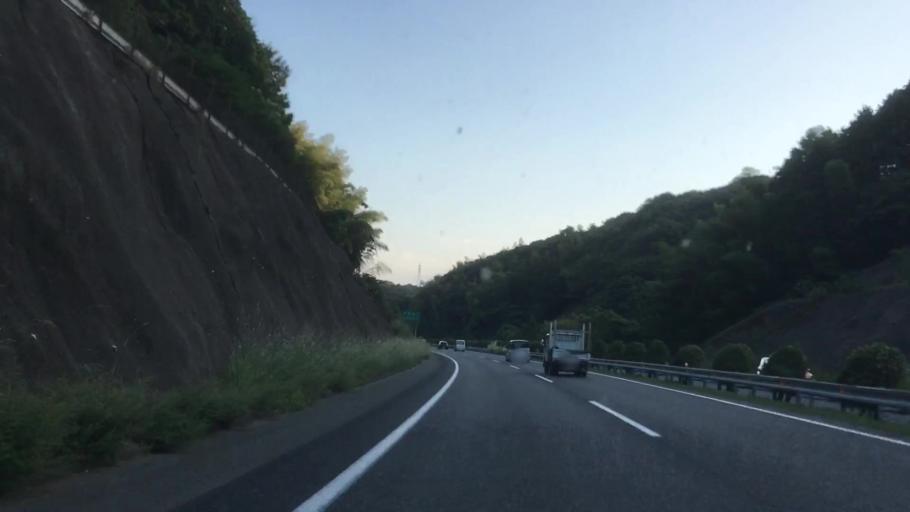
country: JP
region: Yamaguchi
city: Shimonoseki
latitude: 33.9030
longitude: 130.9714
